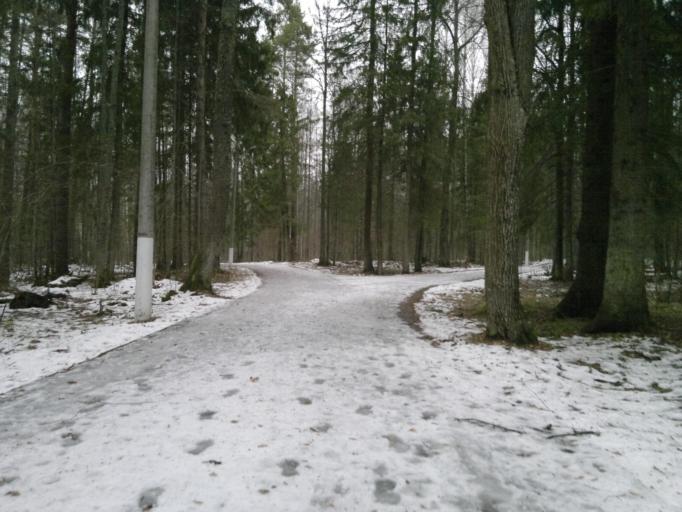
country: RU
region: Mariy-El
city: Yoshkar-Ola
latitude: 56.6017
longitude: 47.9647
